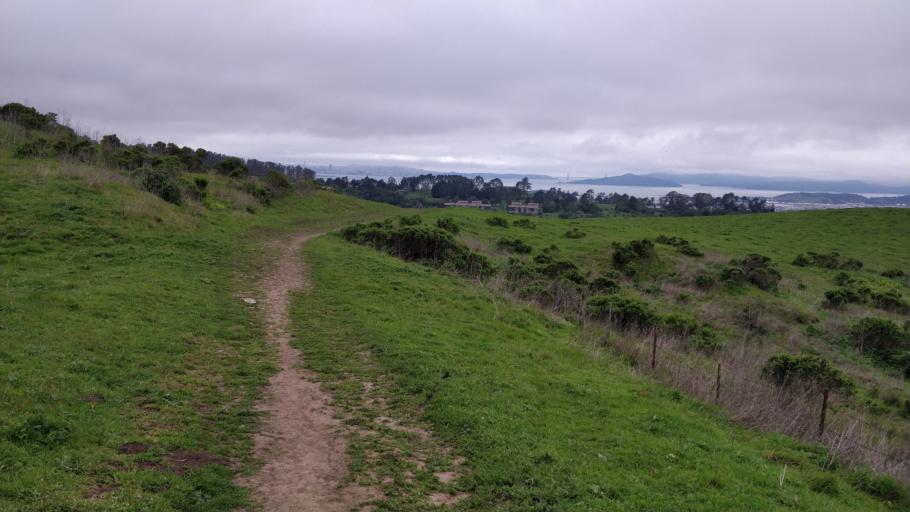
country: US
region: California
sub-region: Contra Costa County
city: East Richmond Heights
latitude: 37.9441
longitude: -122.2919
